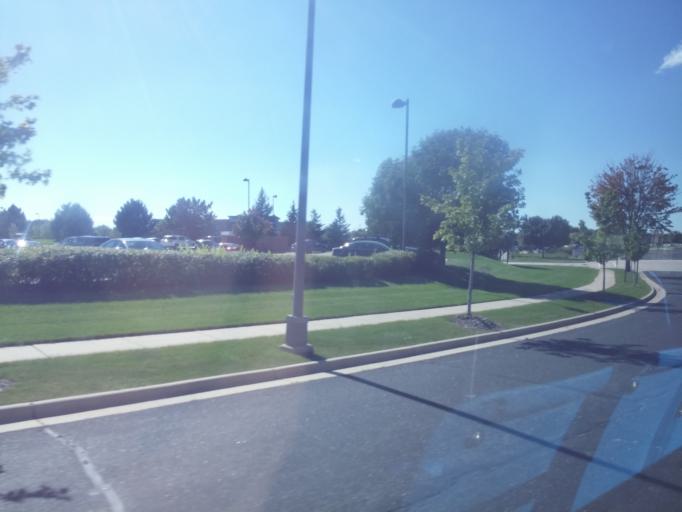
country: US
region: Wisconsin
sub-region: Dane County
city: Sun Prairie
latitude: 43.1458
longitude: -89.2906
